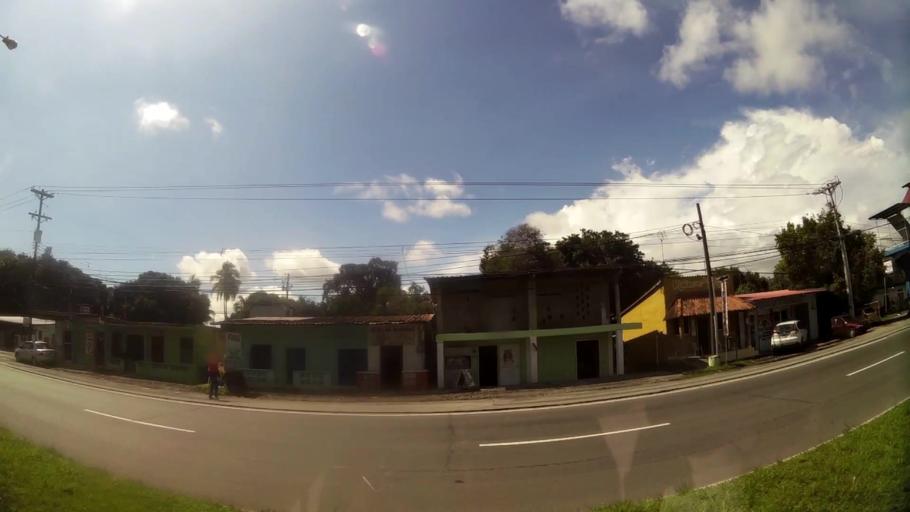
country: PA
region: Panama
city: Bejuco
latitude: 8.6016
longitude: -79.8885
